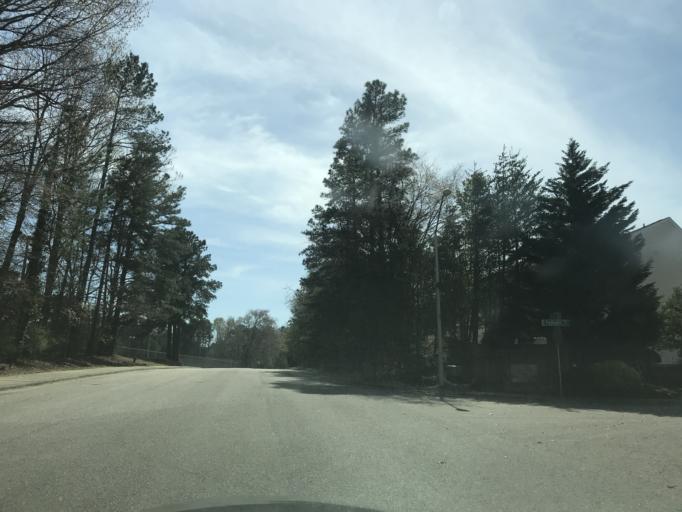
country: US
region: North Carolina
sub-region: Wake County
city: Raleigh
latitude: 35.8424
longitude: -78.5933
